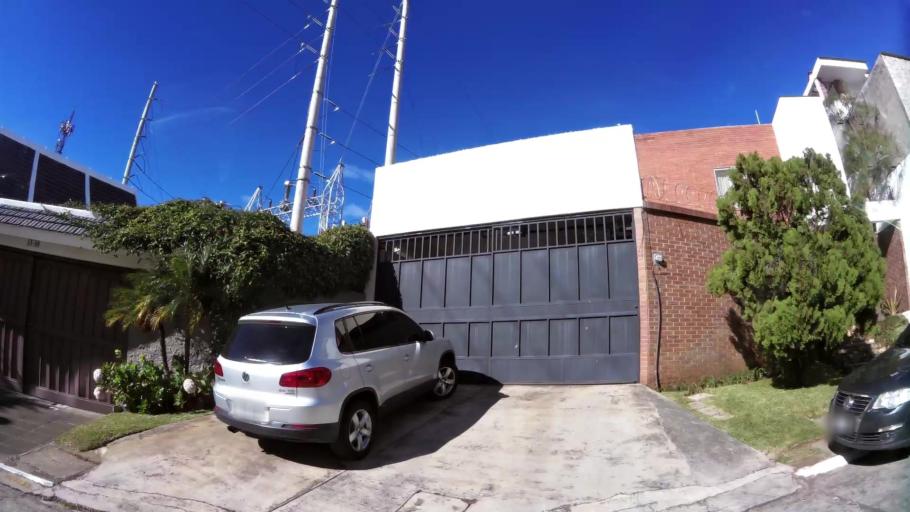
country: GT
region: Guatemala
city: Santa Catarina Pinula
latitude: 14.5661
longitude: -90.5279
